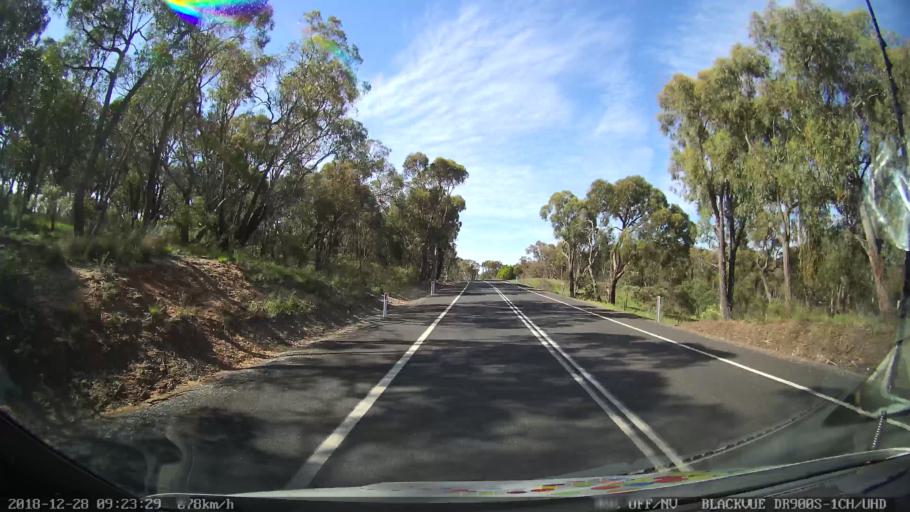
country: AU
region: New South Wales
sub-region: Upper Lachlan Shire
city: Crookwell
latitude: -34.3860
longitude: 149.3842
